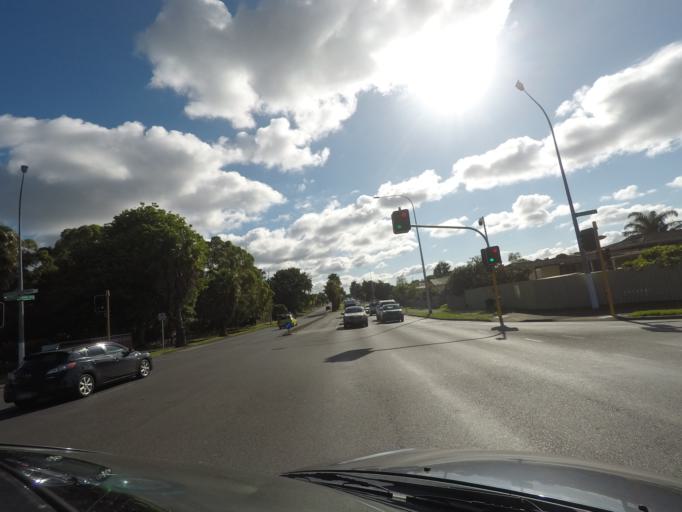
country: NZ
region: Auckland
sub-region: Auckland
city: Manukau City
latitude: -36.9844
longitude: 174.8884
